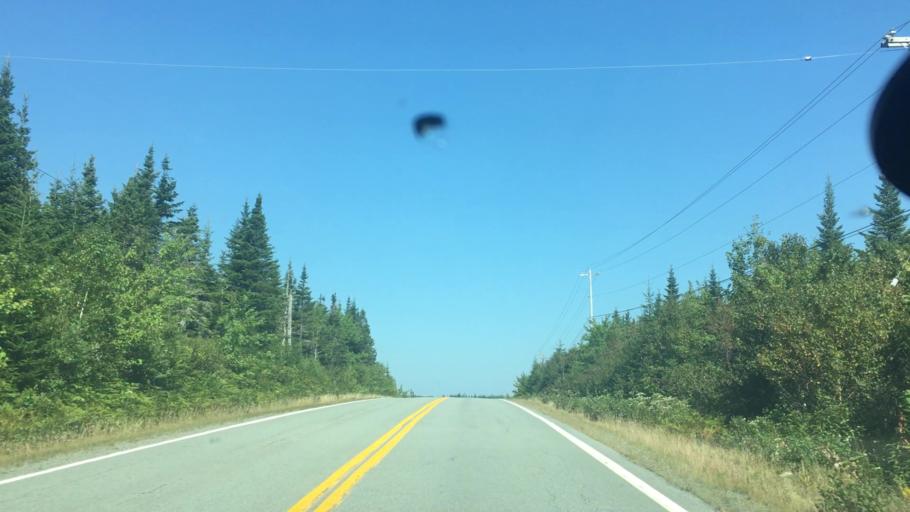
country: CA
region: Nova Scotia
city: Antigonish
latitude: 45.0090
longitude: -62.1057
